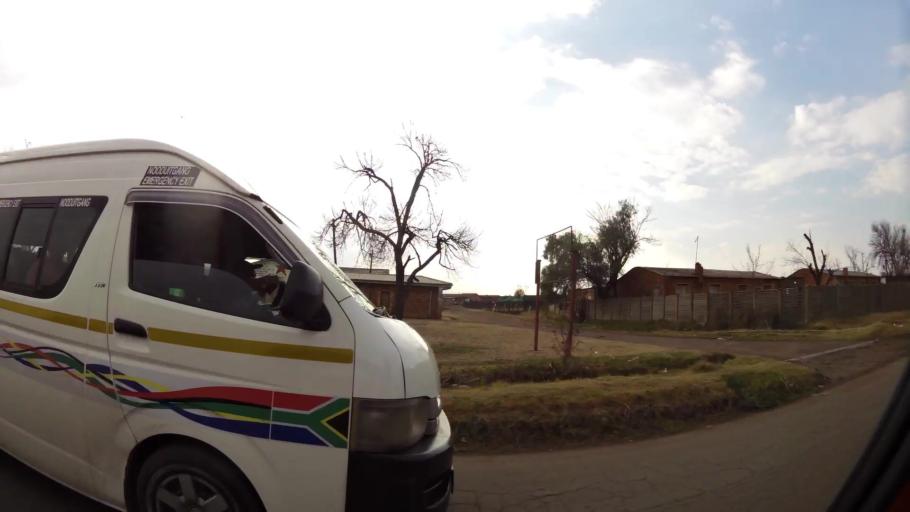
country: ZA
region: Gauteng
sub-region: Sedibeng District Municipality
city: Vereeniging
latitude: -26.6775
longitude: 27.8899
